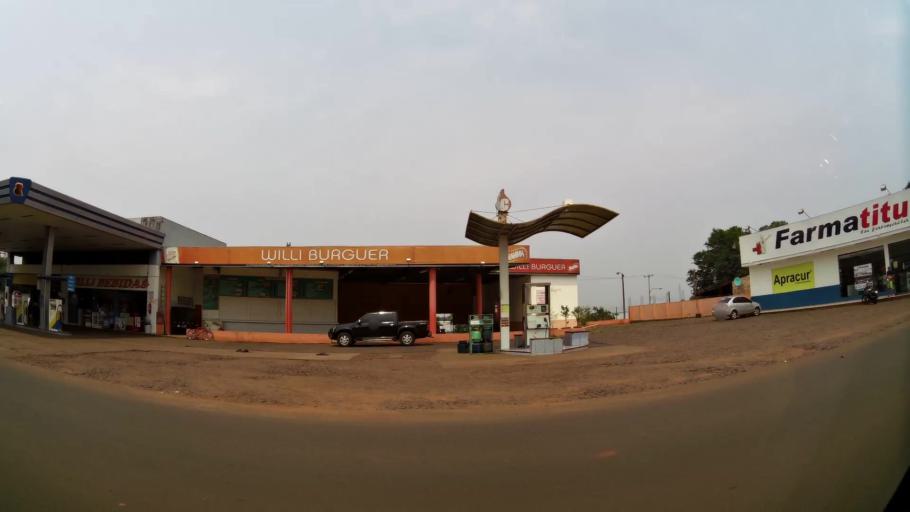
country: PY
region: Alto Parana
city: Presidente Franco
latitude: -25.5581
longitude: -54.6223
